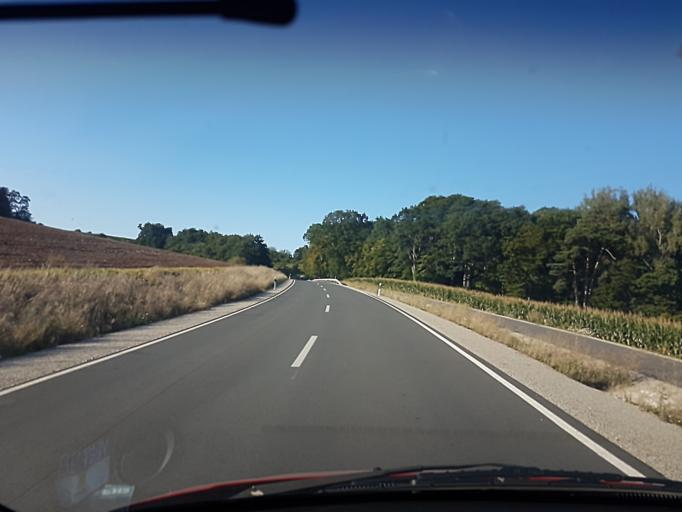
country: DE
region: Bavaria
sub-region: Upper Franconia
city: Hallerndorf
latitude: 49.7583
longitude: 10.9469
